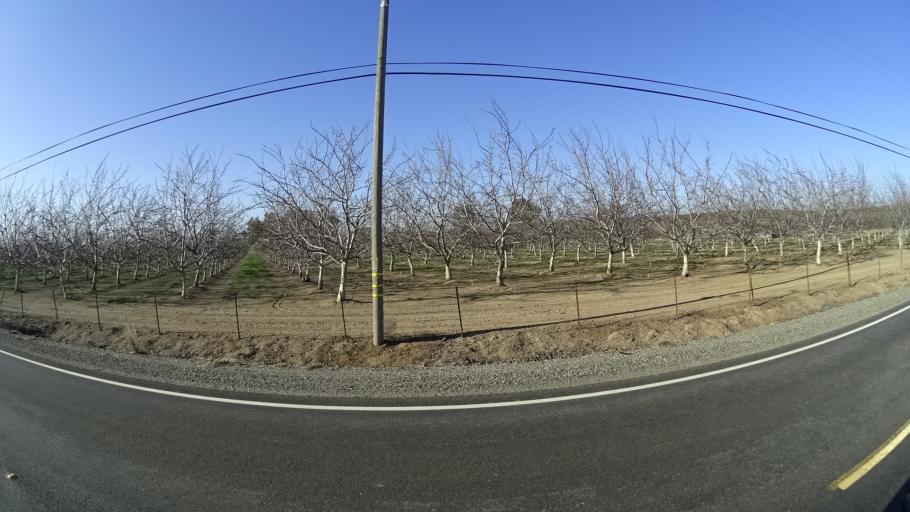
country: US
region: California
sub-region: Glenn County
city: Orland
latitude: 39.7773
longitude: -122.2788
